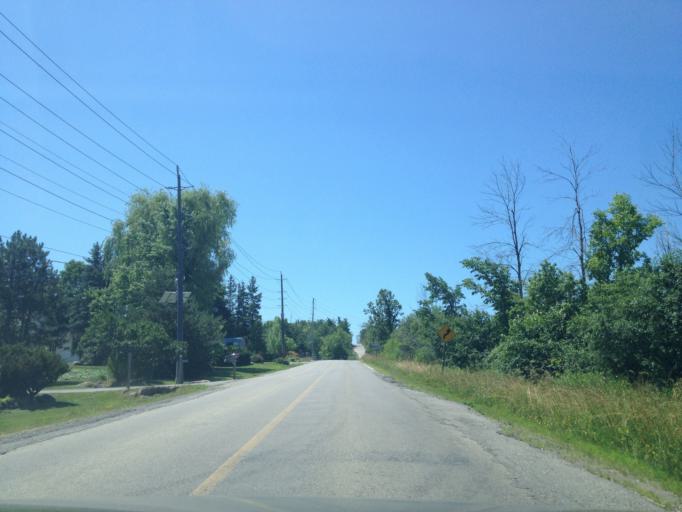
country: CA
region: Ontario
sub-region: Halton
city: Milton
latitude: 43.6626
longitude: -79.9514
